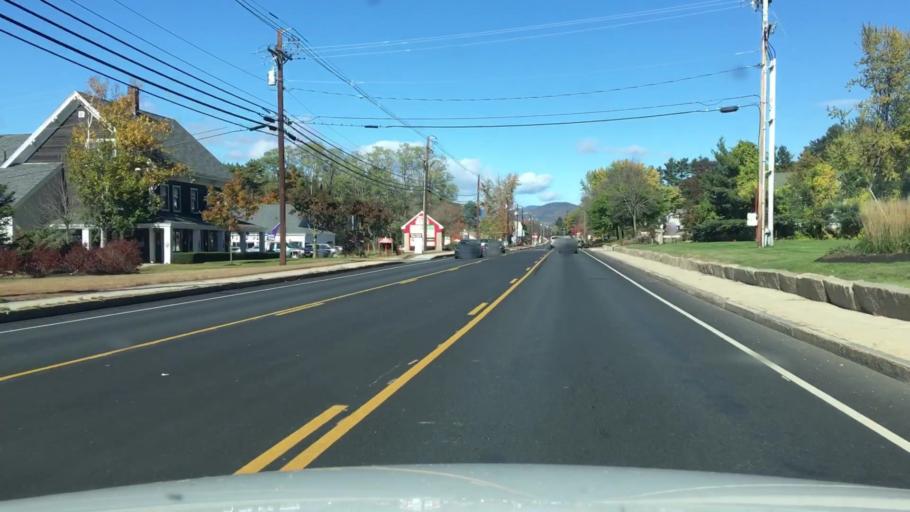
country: US
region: New Hampshire
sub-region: Carroll County
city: North Conway
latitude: 44.0326
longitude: -71.1208
